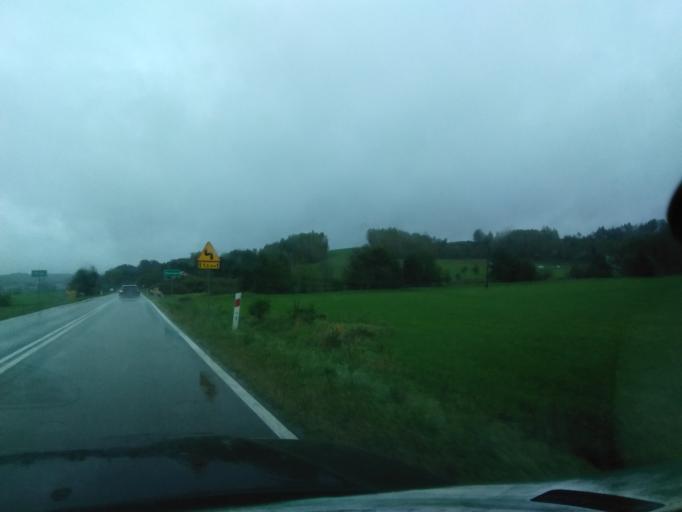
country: PL
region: Subcarpathian Voivodeship
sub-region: Powiat ropczycko-sedziszowski
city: Niedzwiada
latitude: 49.9830
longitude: 21.5598
